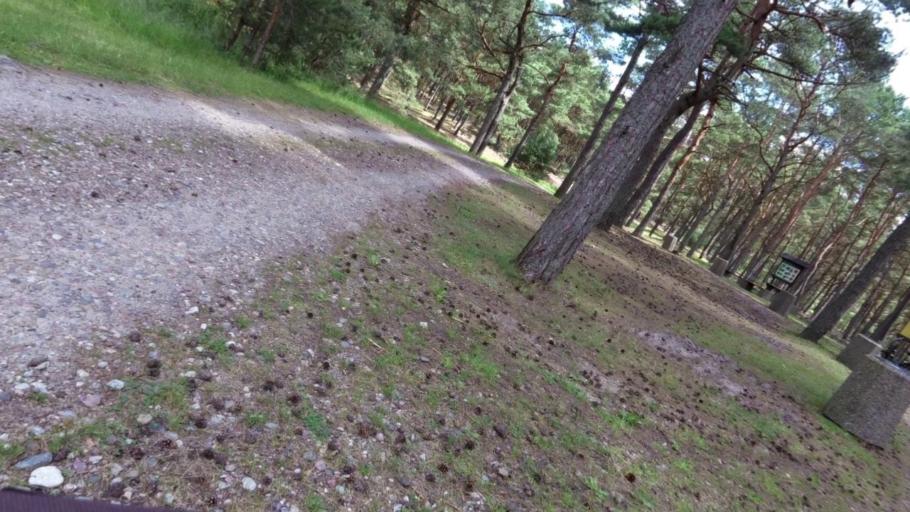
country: PL
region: West Pomeranian Voivodeship
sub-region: Powiat gryficki
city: Mrzezyno
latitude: 54.1251
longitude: 15.2366
